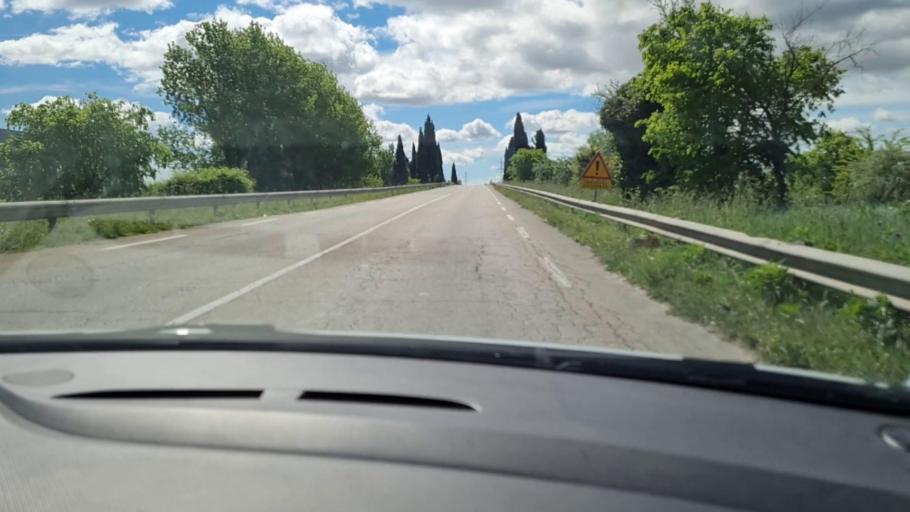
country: FR
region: Languedoc-Roussillon
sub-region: Departement du Gard
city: Milhaud
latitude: 43.8082
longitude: 4.3334
